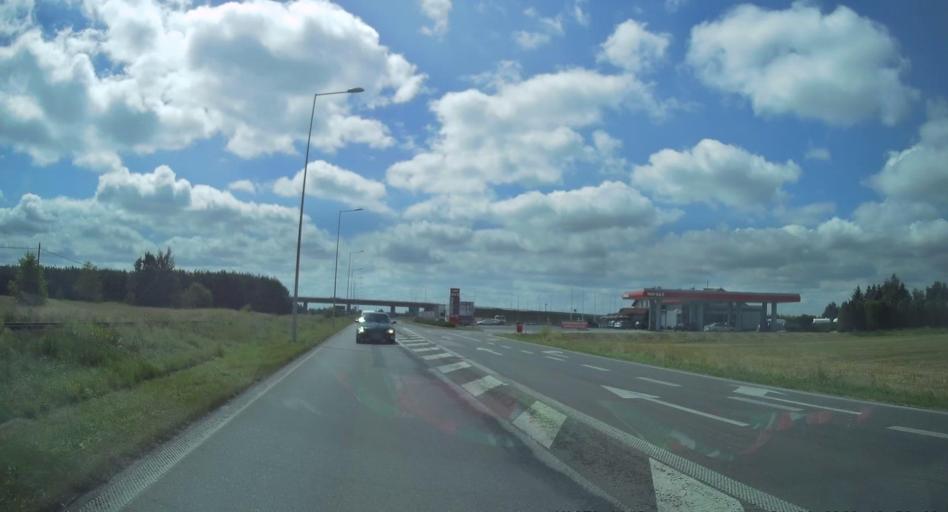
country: PL
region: Subcarpathian Voivodeship
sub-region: Powiat mielecki
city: Padew Narodowa
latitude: 50.3856
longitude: 21.4604
